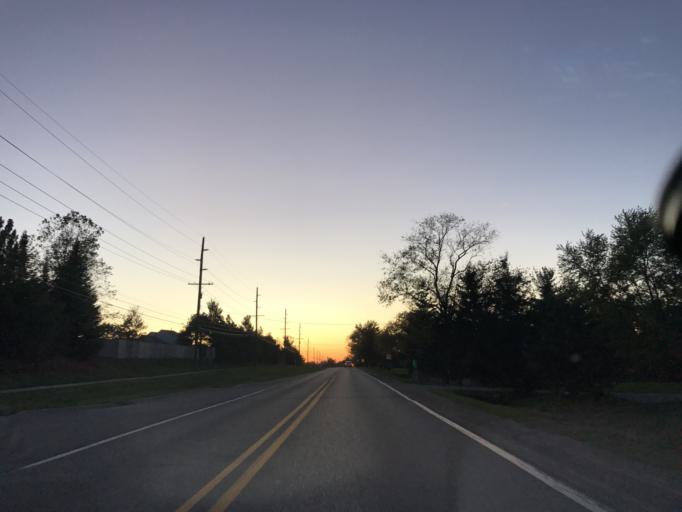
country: US
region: Michigan
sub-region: Oakland County
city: South Lyon
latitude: 42.4756
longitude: -83.6394
